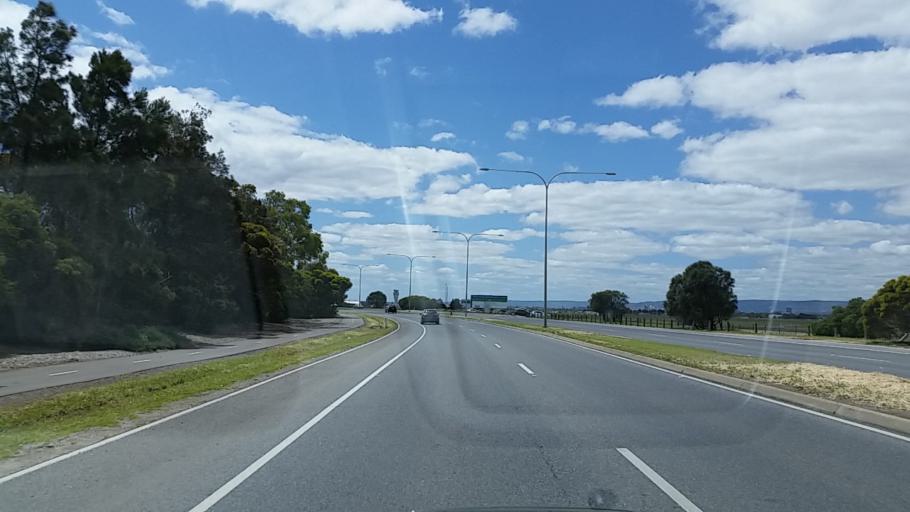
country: AU
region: South Australia
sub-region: Holdfast Bay
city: Glenelg East
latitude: -34.9553
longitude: 138.5162
